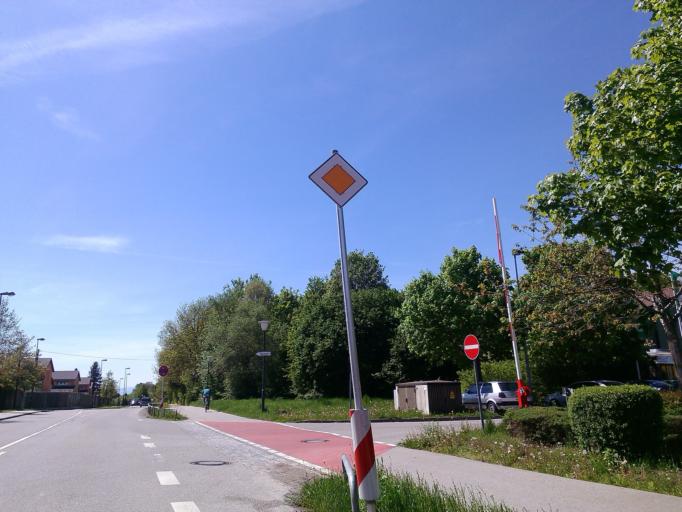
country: DE
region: Bavaria
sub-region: Upper Bavaria
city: Starnberg
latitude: 48.0130
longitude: 11.3491
